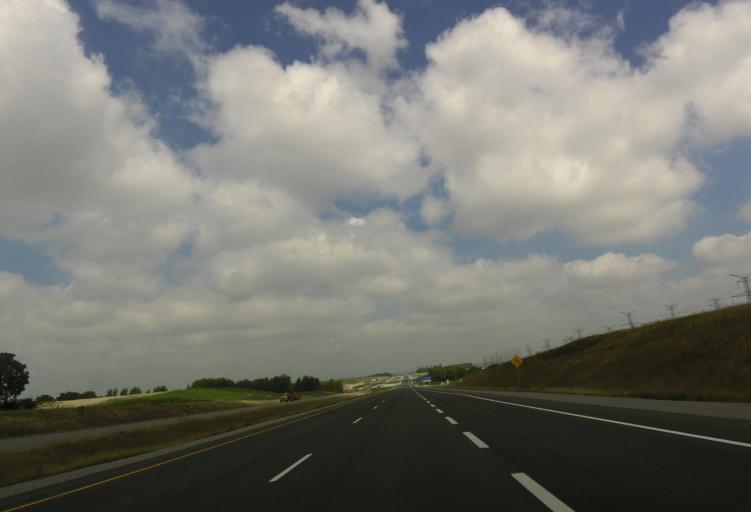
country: CA
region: Ontario
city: Oshawa
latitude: 43.9558
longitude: -78.9319
